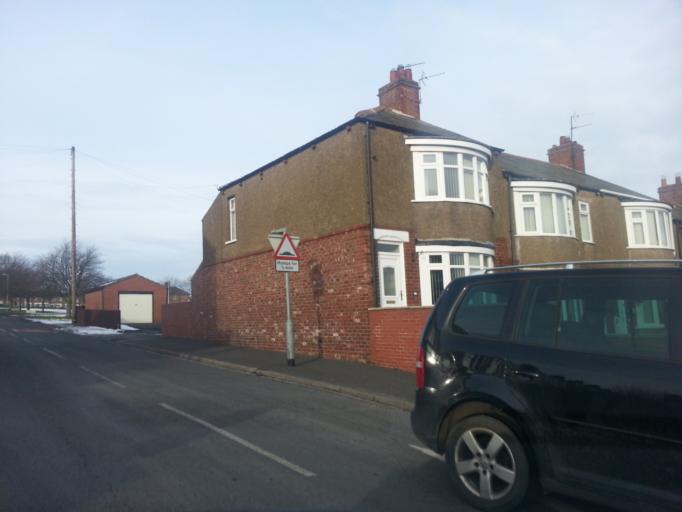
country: GB
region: England
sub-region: County Durham
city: Crook
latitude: 54.7126
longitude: -1.7544
